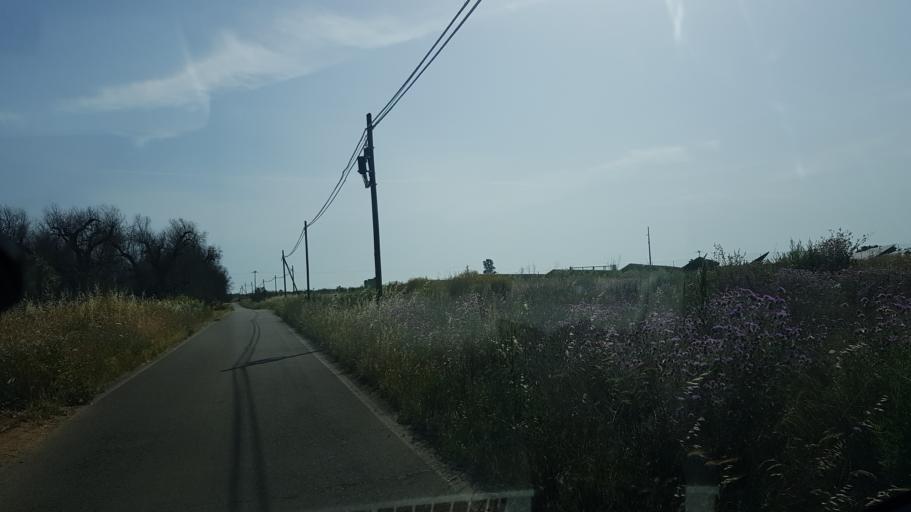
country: IT
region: Apulia
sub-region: Provincia di Brindisi
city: Torchiarolo
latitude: 40.5115
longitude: 18.0756
